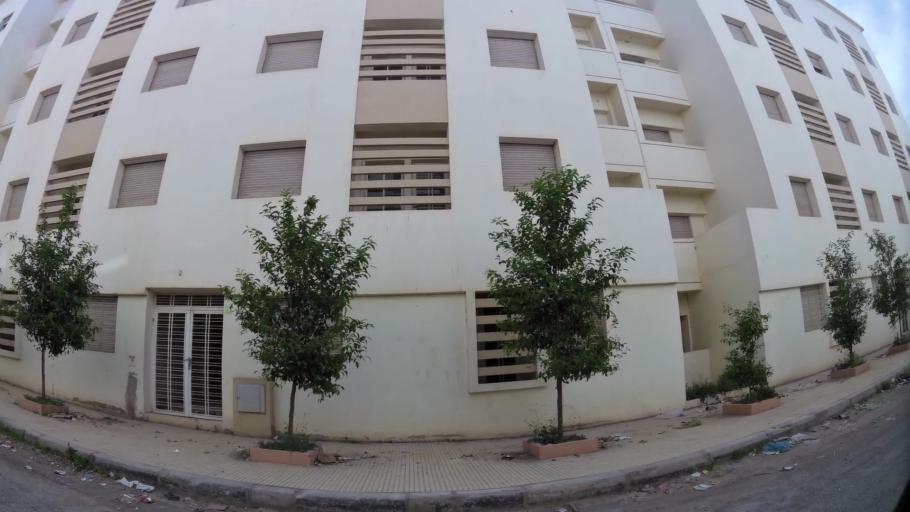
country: MA
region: Fes-Boulemane
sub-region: Fes
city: Fes
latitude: 34.0103
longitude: -5.0414
